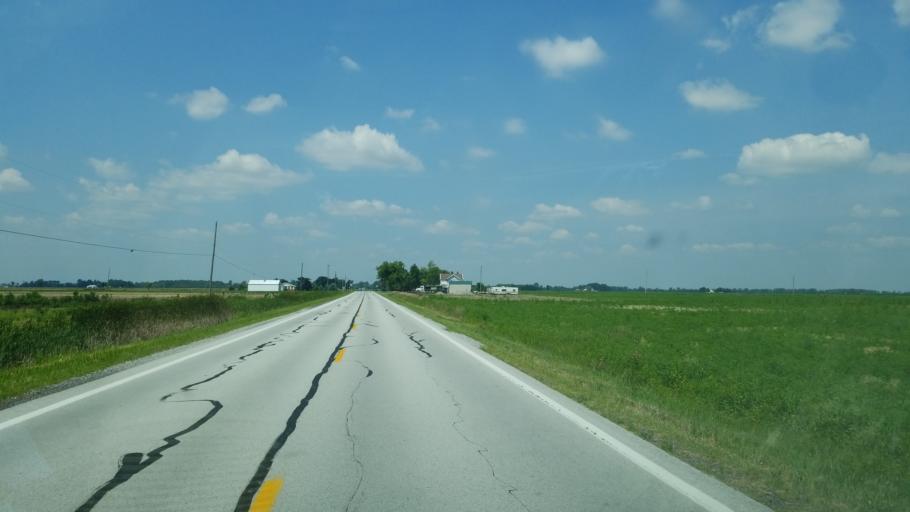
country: US
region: Ohio
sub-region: Henry County
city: Deshler
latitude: 41.2847
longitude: -83.8598
